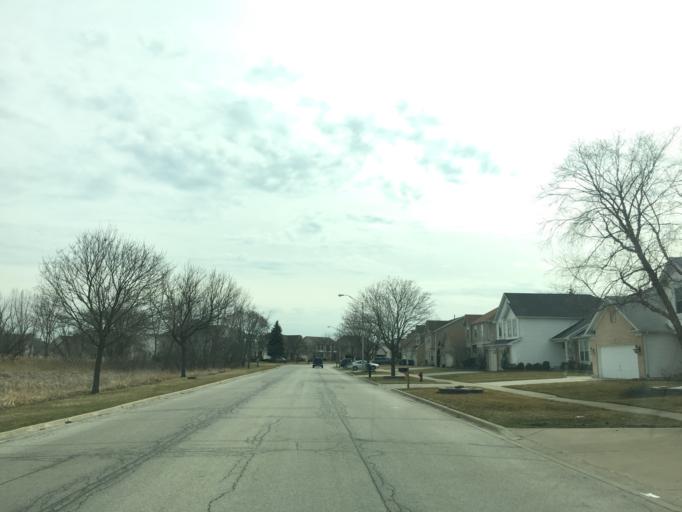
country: US
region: Illinois
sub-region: Cook County
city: Schaumburg
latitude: 42.0454
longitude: -88.1200
